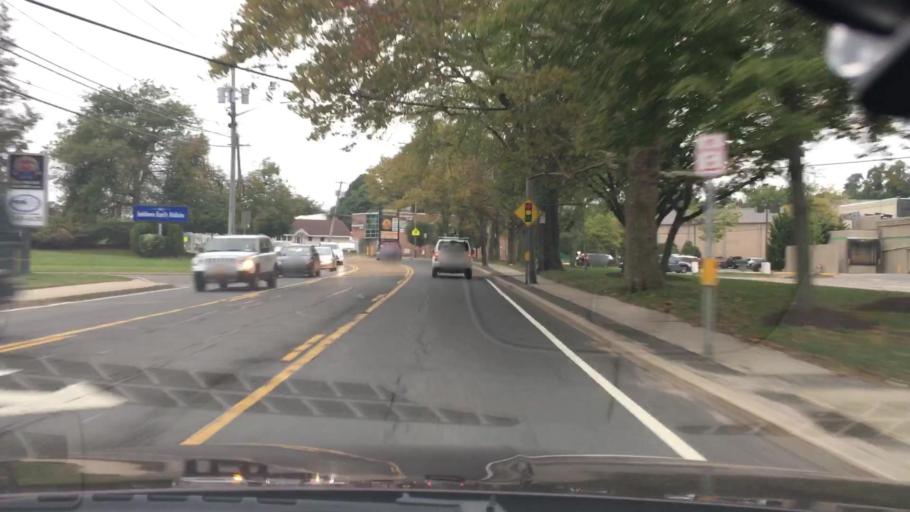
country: US
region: New York
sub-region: Suffolk County
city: Hauppauge
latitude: 40.8275
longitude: -73.2006
